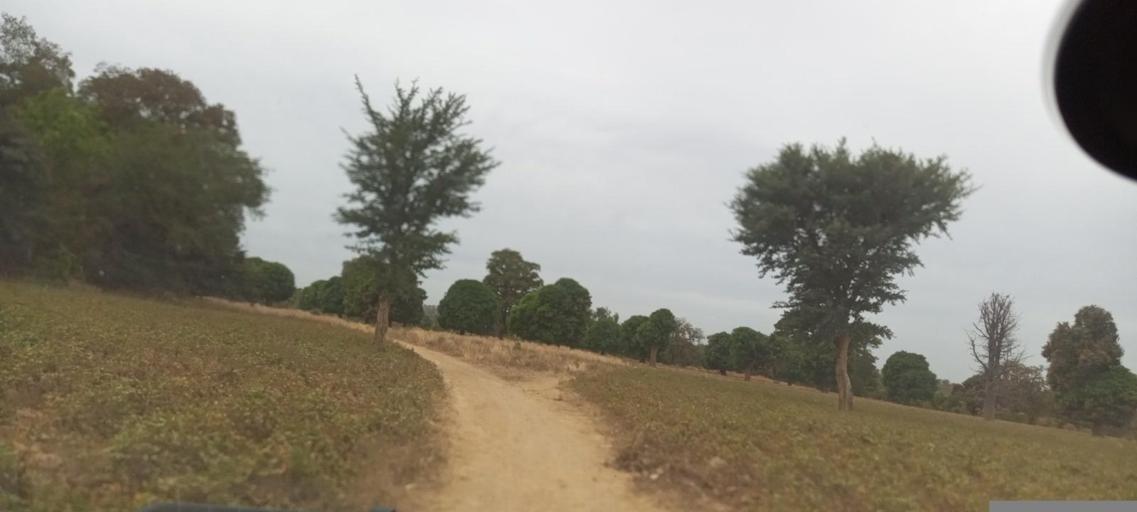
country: ML
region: Koulikoro
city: Kati
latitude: 12.7702
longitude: -8.3705
